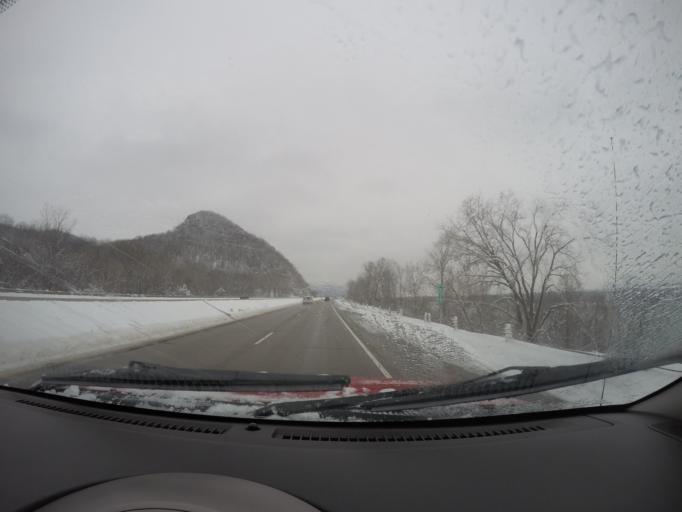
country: US
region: Minnesota
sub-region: Houston County
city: La Crescent
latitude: 43.8741
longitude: -91.3210
